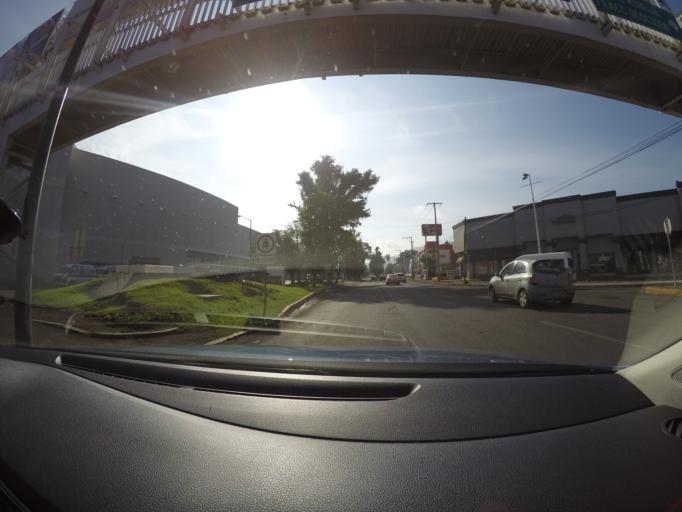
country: MX
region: Michoacan
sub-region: Morelia
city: Montana Monarca (Punta Altozano)
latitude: 19.6877
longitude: -101.1588
